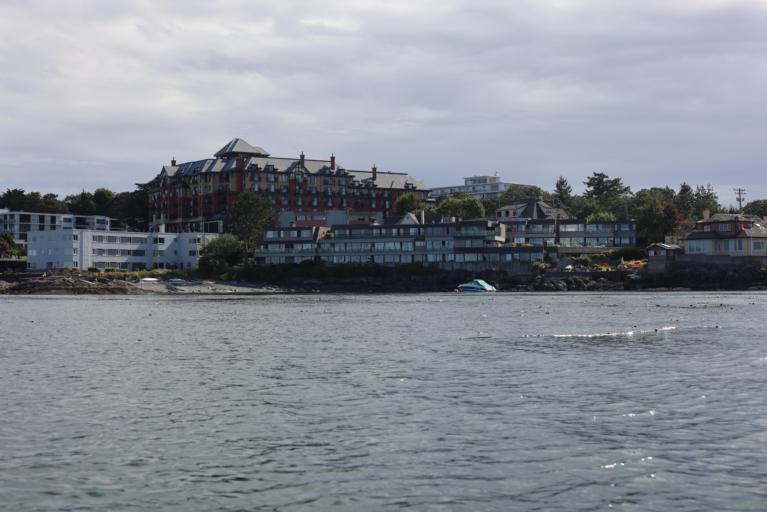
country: CA
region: British Columbia
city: Oak Bay
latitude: 48.4225
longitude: -123.2961
